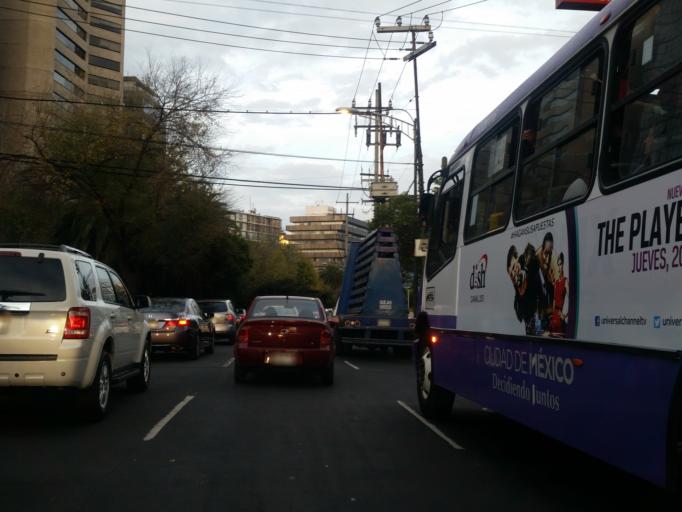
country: MX
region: Mexico City
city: Miguel Hidalgo
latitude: 19.4290
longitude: -99.2160
